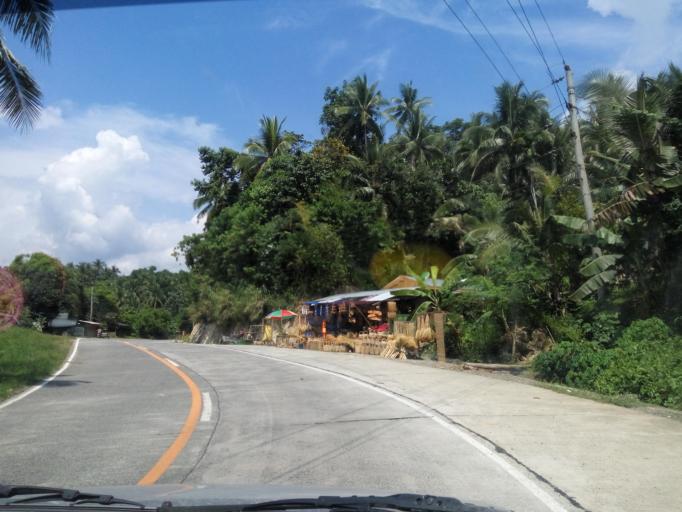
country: PH
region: Central Luzon
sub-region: Province of Aurora
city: Maria Aurora
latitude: 15.7537
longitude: 121.4192
